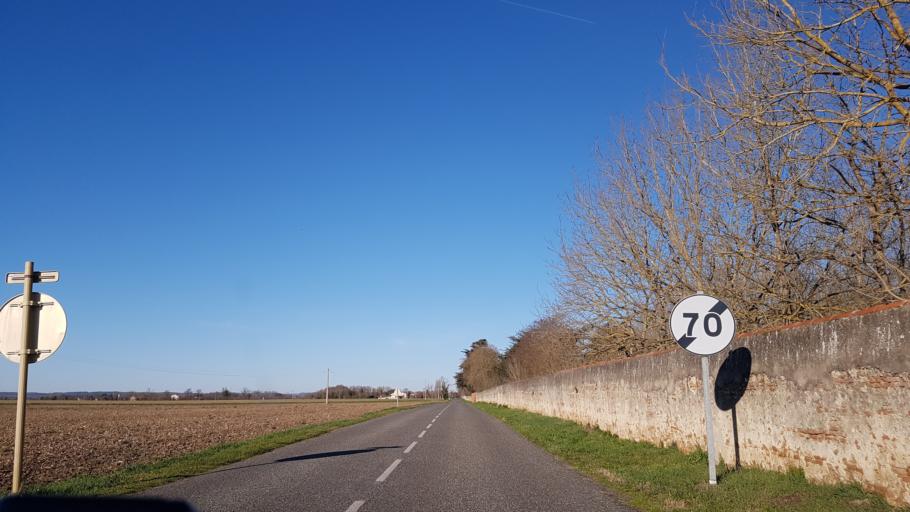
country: FR
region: Midi-Pyrenees
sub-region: Departement de la Haute-Garonne
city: Calmont
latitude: 43.2894
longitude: 1.5999
